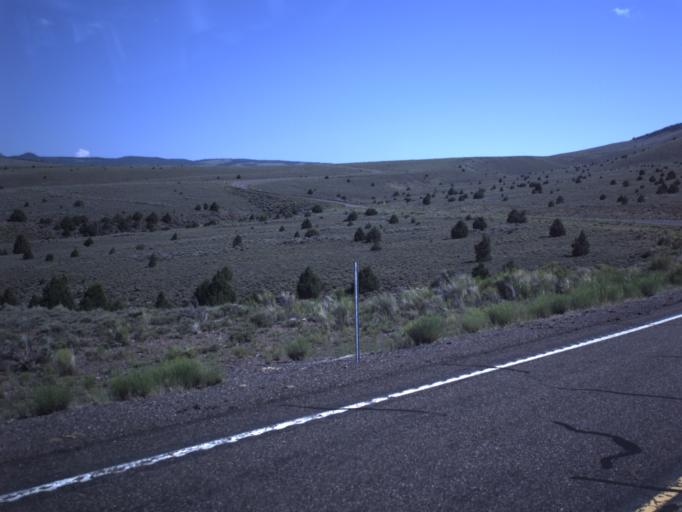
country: US
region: Utah
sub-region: Wayne County
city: Loa
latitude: 38.5288
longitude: -111.5158
